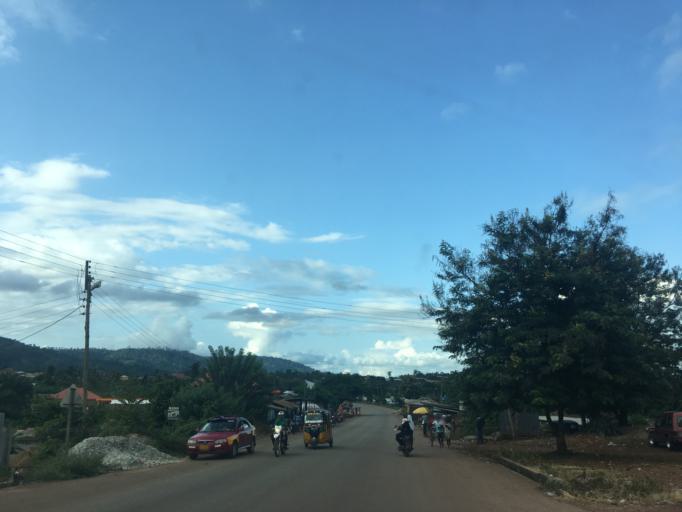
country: GH
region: Western
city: Bibiani
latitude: 6.1978
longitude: -2.3194
